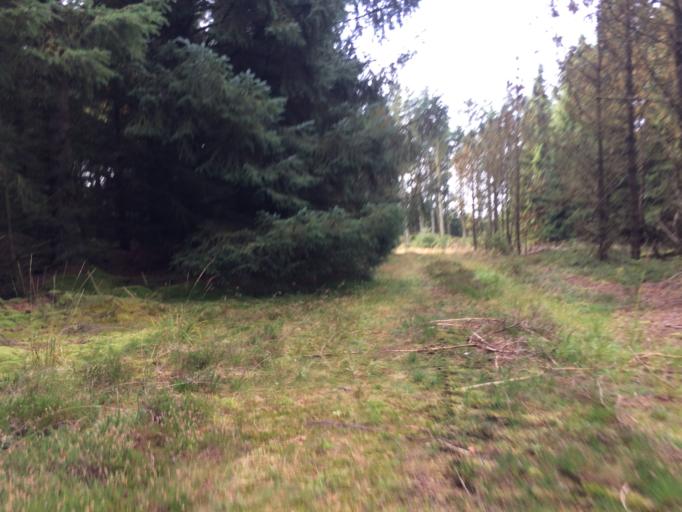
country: DK
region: Central Jutland
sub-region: Holstebro Kommune
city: Ulfborg
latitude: 56.2539
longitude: 8.4268
